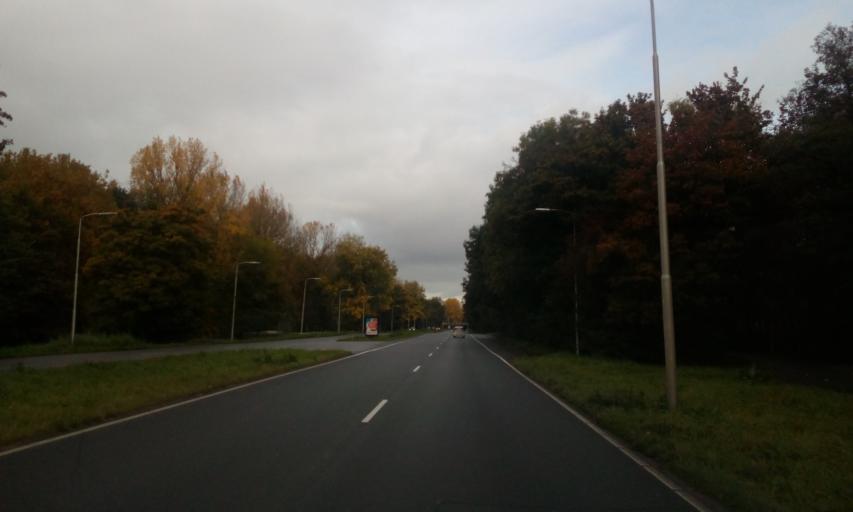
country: NL
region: South Holland
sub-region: Gemeente Delft
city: Delft
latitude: 51.9909
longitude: 4.3507
